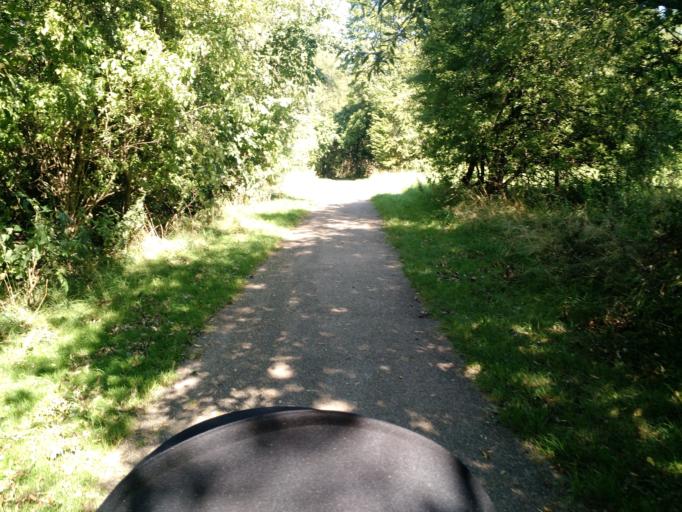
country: DK
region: Capital Region
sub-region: Herlev Kommune
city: Herlev
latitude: 55.7507
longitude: 12.4247
